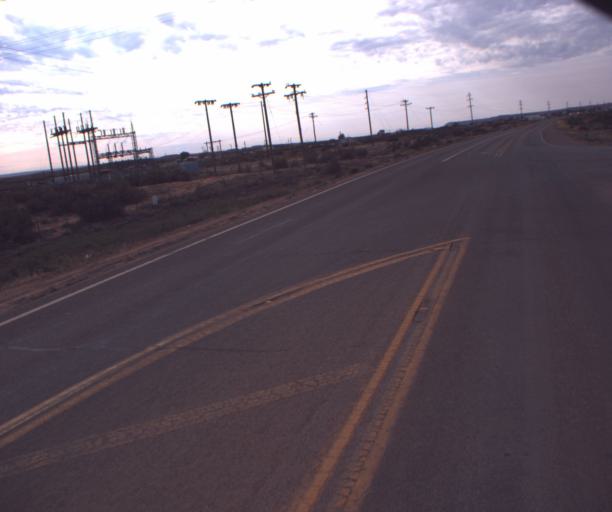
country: US
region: Arizona
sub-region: Apache County
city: Many Farms
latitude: 36.3643
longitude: -109.6140
